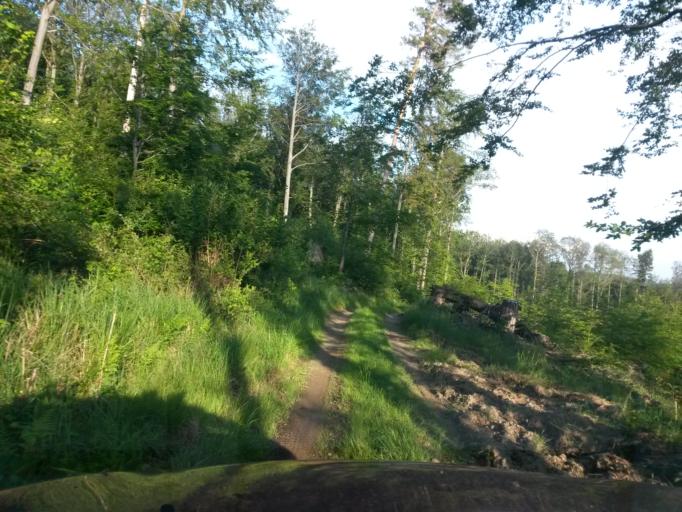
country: SK
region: Kosicky
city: Moldava nad Bodvou
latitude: 48.7348
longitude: 21.0412
